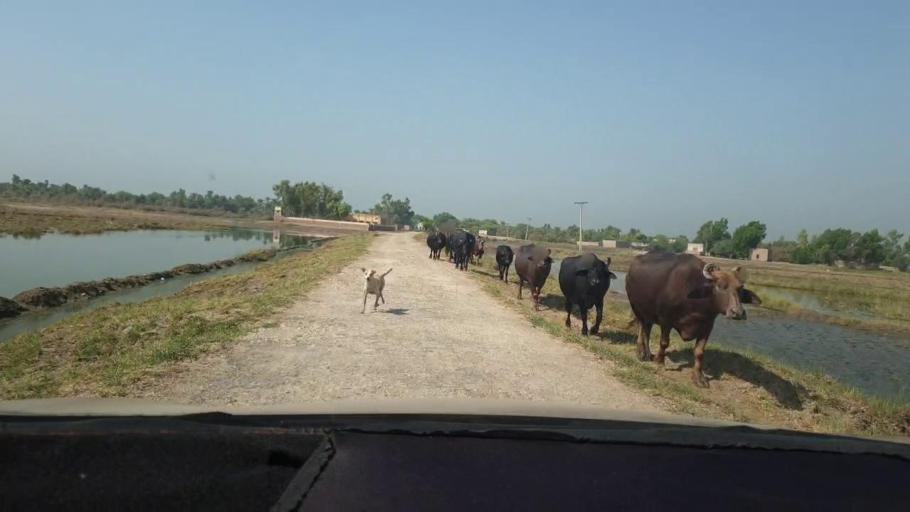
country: PK
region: Sindh
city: Miro Khan
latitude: 27.7084
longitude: 68.0982
